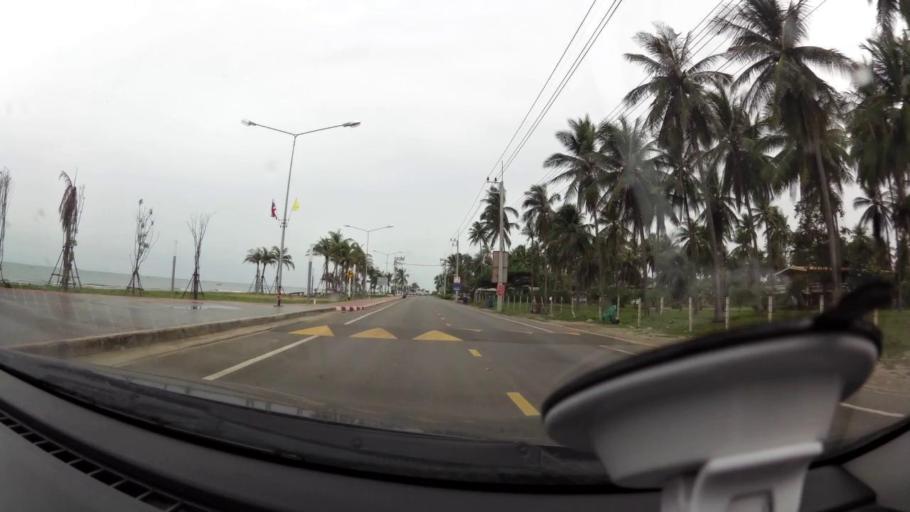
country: TH
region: Prachuap Khiri Khan
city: Pran Buri
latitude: 12.3887
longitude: 99.9979
